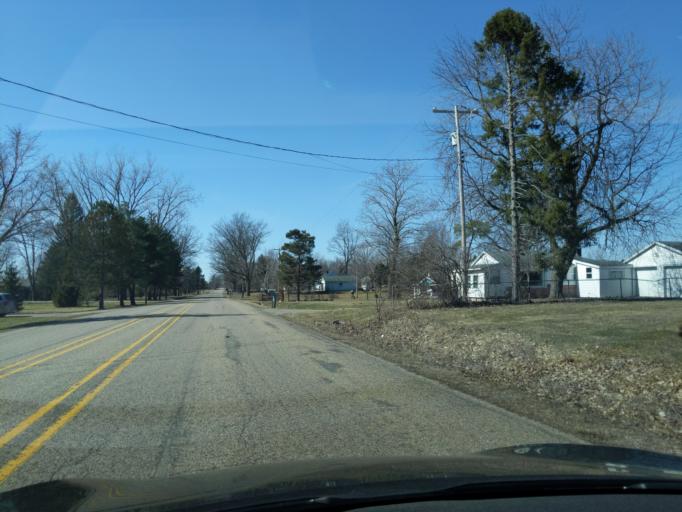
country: US
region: Michigan
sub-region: Eaton County
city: Grand Ledge
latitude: 42.7264
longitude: -84.7423
